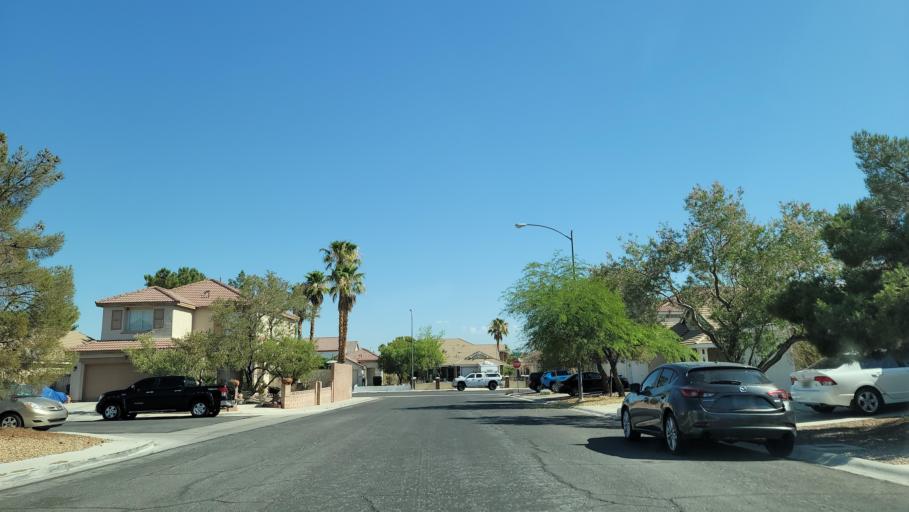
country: US
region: Nevada
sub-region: Clark County
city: Spring Valley
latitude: 36.0862
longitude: -115.2558
